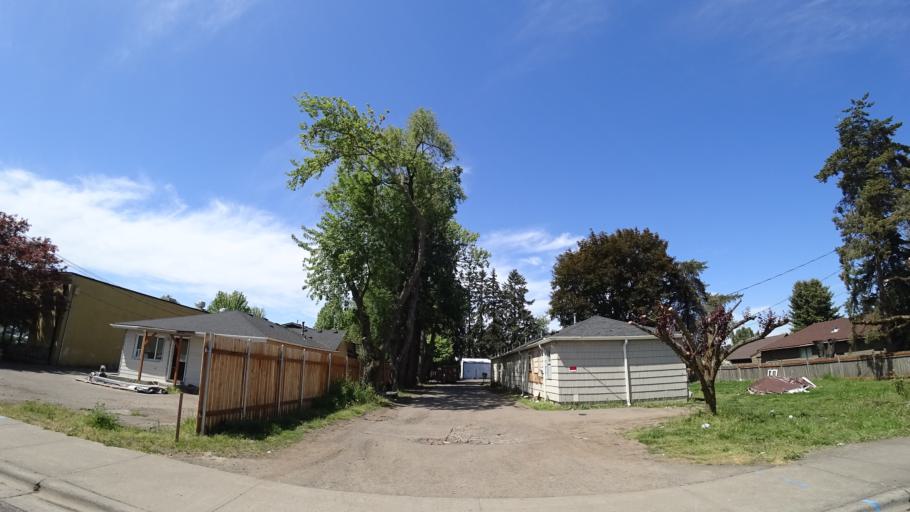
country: US
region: Oregon
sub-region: Washington County
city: Aloha
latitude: 45.4988
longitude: -122.9023
